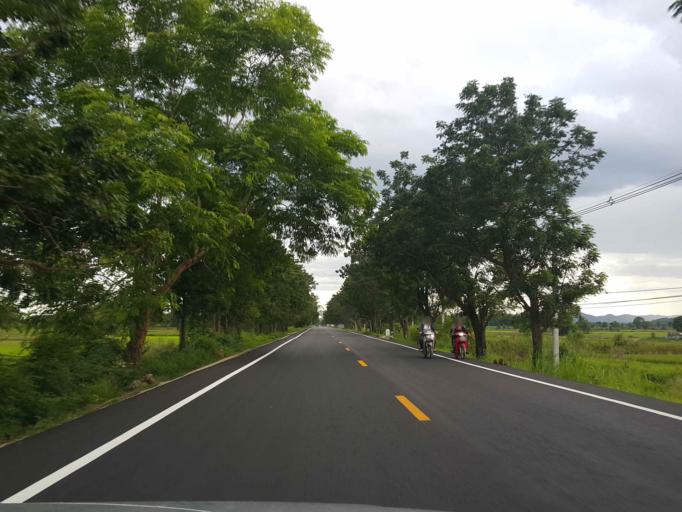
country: TH
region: Sukhothai
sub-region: Amphoe Si Satchanalai
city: Si Satchanalai
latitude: 17.4828
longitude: 99.7438
